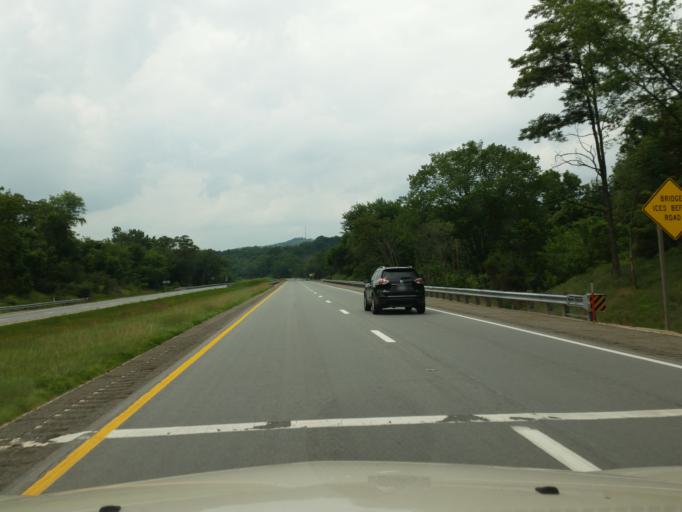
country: US
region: Pennsylvania
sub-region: Perry County
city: Newport
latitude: 40.5362
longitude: -77.1417
